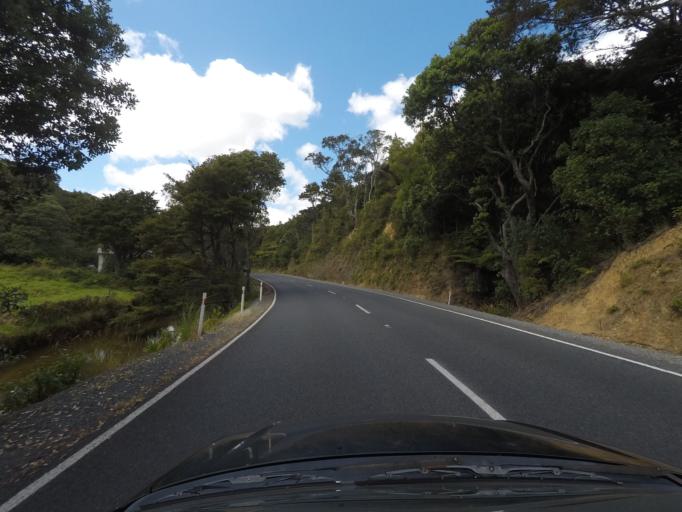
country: NZ
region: Northland
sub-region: Whangarei
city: Ruakaka
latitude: -36.0318
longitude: 174.5092
